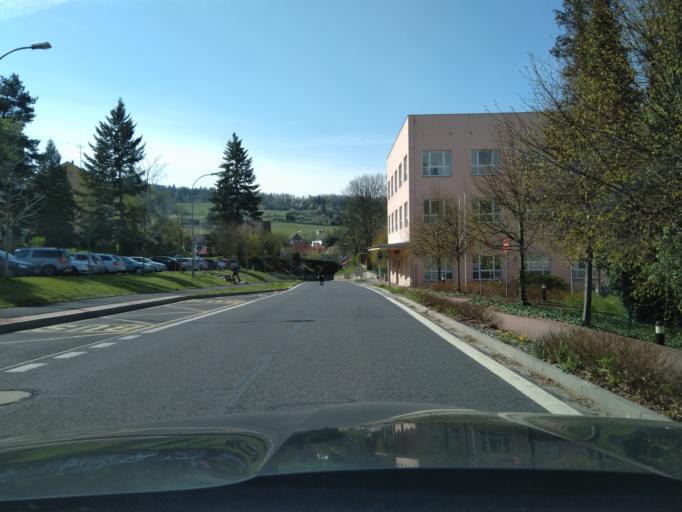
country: CZ
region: Plzensky
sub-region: Okres Klatovy
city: Susice
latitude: 49.2305
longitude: 13.5270
